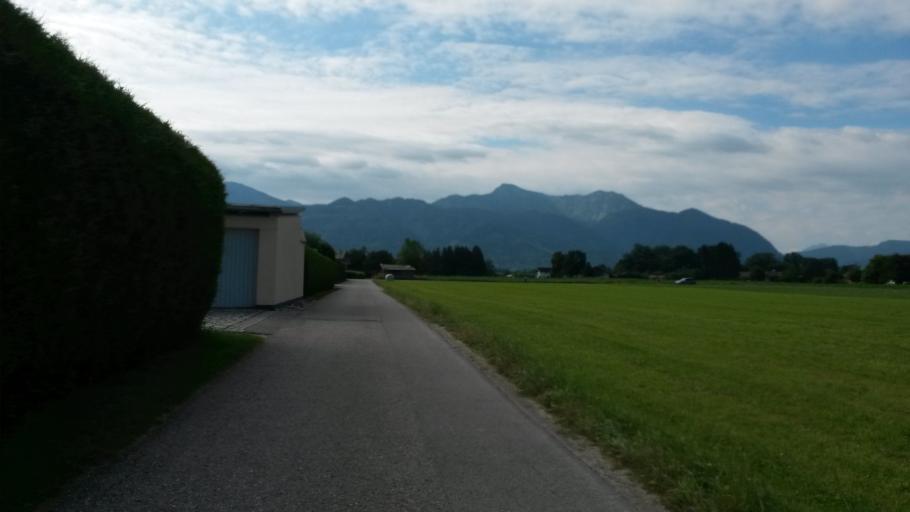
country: DE
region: Bavaria
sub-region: Upper Bavaria
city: Ubersee
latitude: 47.8320
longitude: 12.4884
